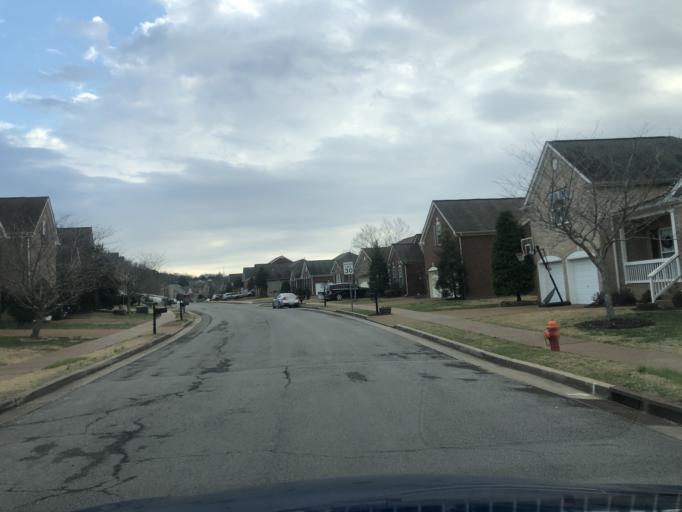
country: US
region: Tennessee
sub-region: Davidson County
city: Belle Meade
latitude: 36.1184
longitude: -86.9326
